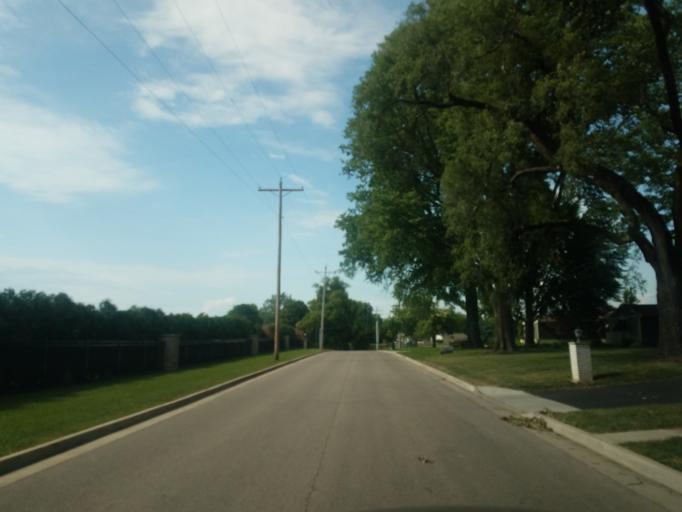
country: US
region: Illinois
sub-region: McLean County
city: Bloomington
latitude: 40.4803
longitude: -88.9627
